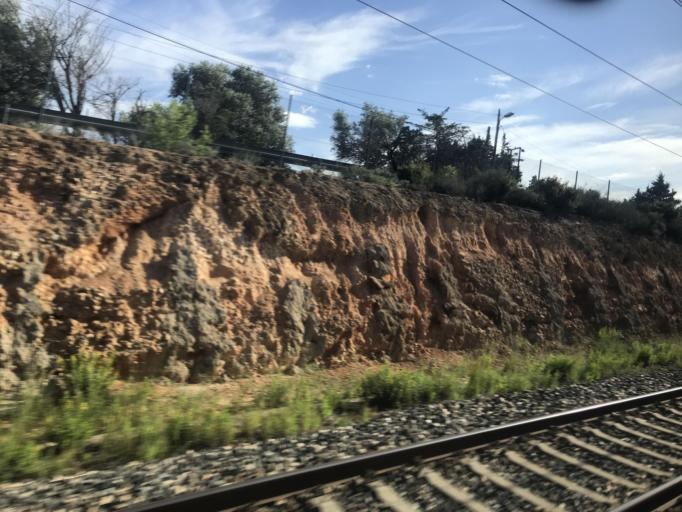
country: ES
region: Catalonia
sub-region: Provincia de Tarragona
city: L'Ampolla
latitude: 40.8265
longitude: 0.7323
